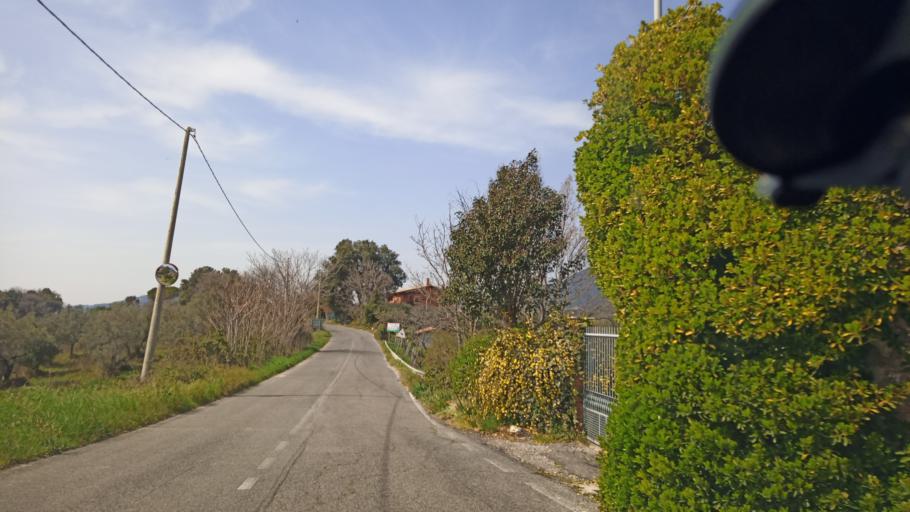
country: IT
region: Latium
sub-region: Provincia di Rieti
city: Montasola
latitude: 42.3647
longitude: 12.6701
